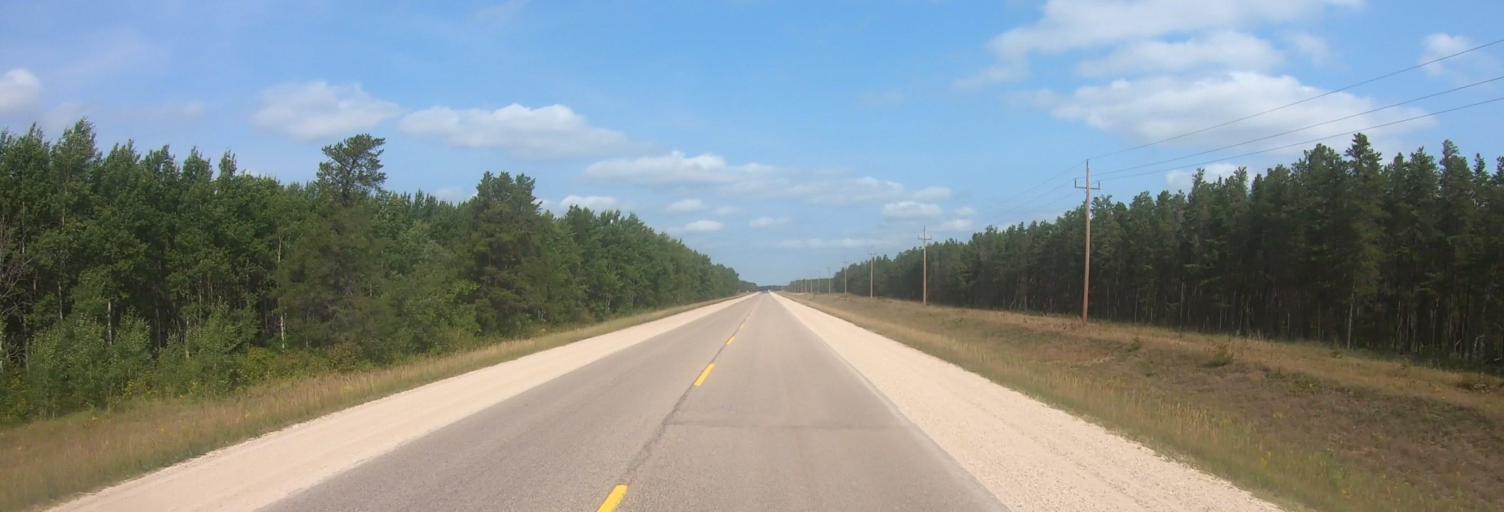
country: CA
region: Manitoba
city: La Broquerie
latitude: 49.2475
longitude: -96.3523
